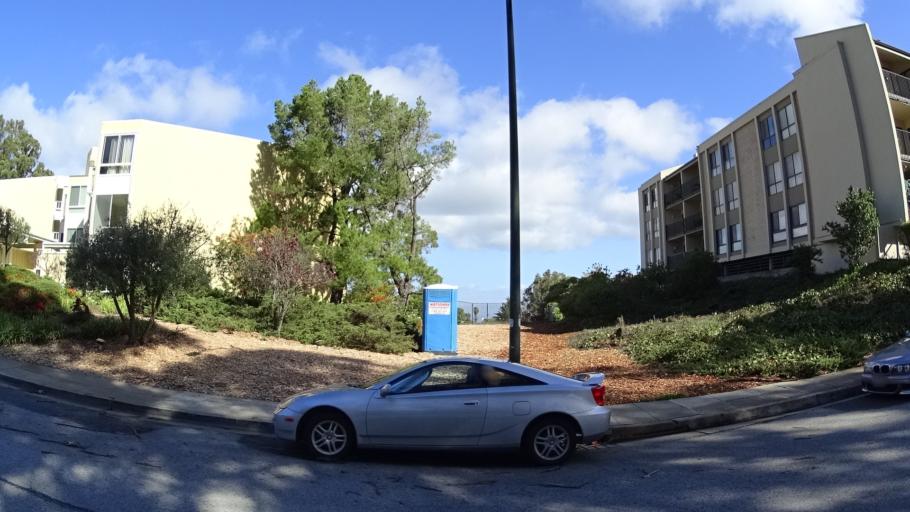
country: US
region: California
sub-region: San Mateo County
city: Millbrae
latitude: 37.5832
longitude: -122.4040
